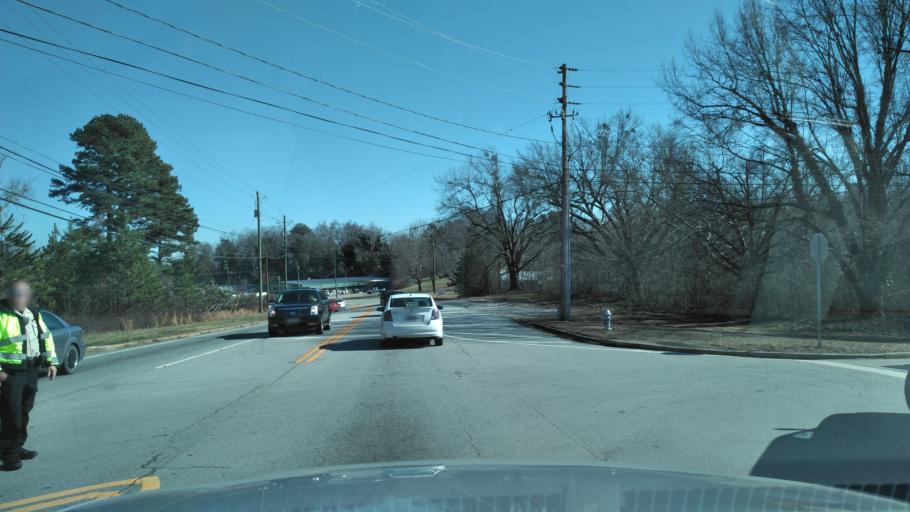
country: US
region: Georgia
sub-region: Hall County
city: Gainesville
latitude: 34.3128
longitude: -83.7743
